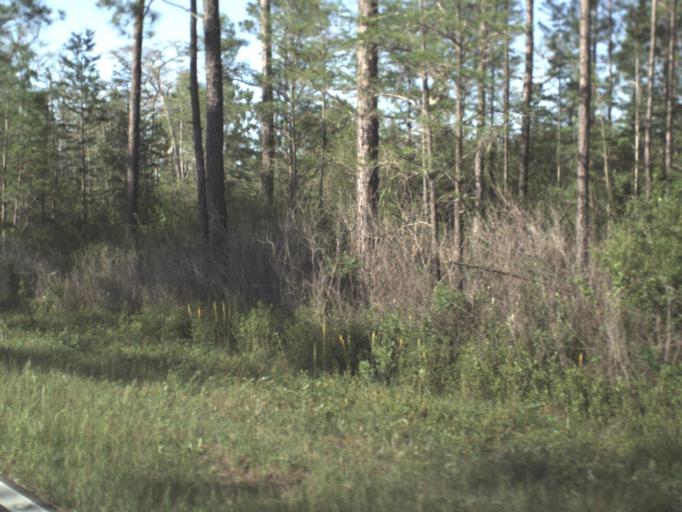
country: US
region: Florida
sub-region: Gulf County
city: Wewahitchka
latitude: 30.0897
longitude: -84.9841
